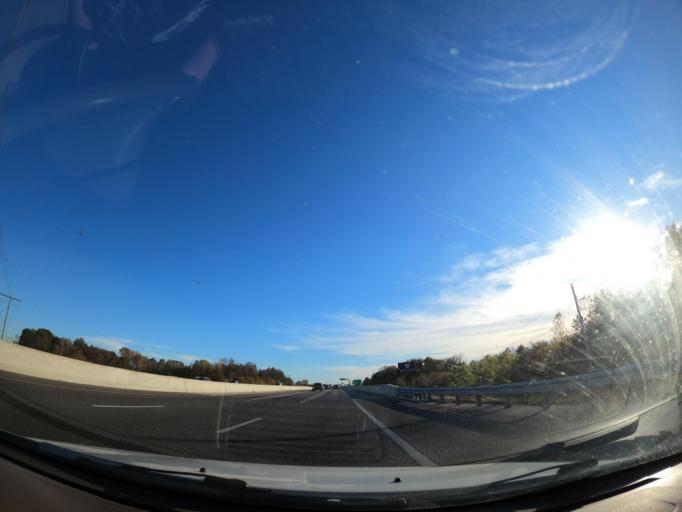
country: US
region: Oklahoma
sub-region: Tulsa County
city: Owasso
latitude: 36.2429
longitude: -95.8483
